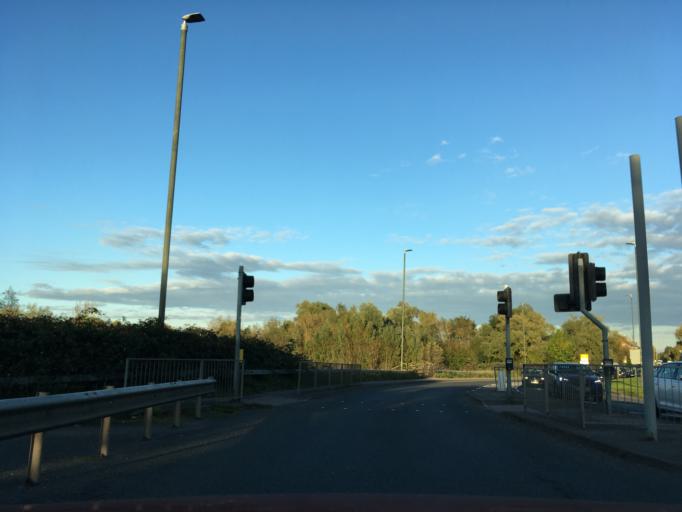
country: GB
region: England
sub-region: Gloucestershire
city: Tewkesbury
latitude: 51.9948
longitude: -2.1452
